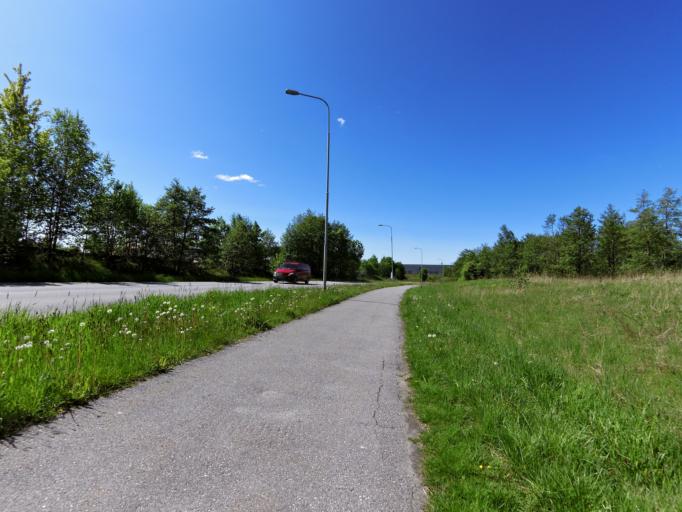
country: NO
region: Ostfold
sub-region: Fredrikstad
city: Fredrikstad
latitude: 59.2398
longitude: 10.9884
